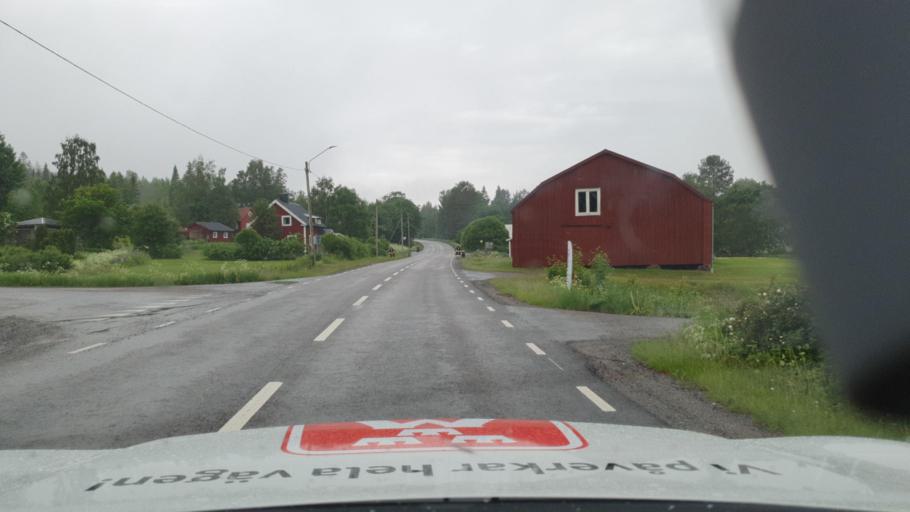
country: SE
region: Vaesterbotten
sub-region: Vannas Kommun
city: Vaennaes
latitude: 63.7817
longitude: 19.8420
